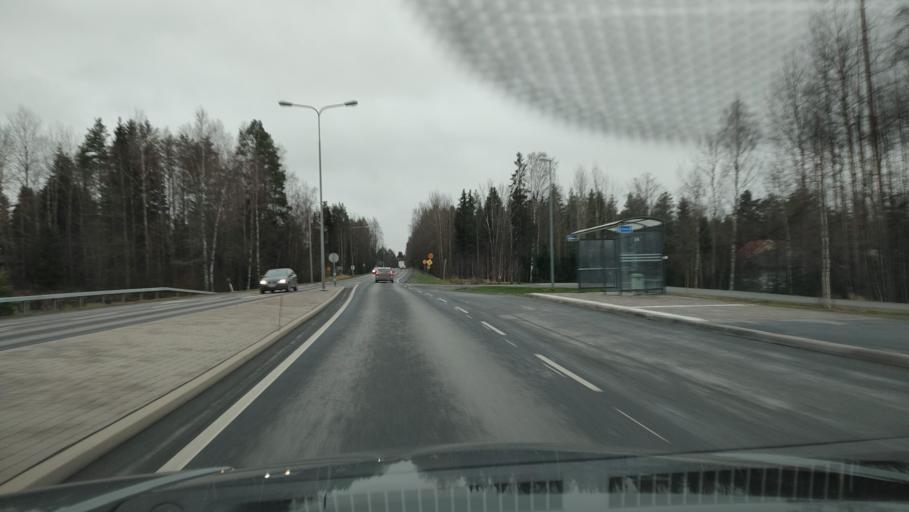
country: FI
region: Southern Ostrobothnia
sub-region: Seinaejoki
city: Ilmajoki
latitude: 62.7700
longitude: 22.6801
